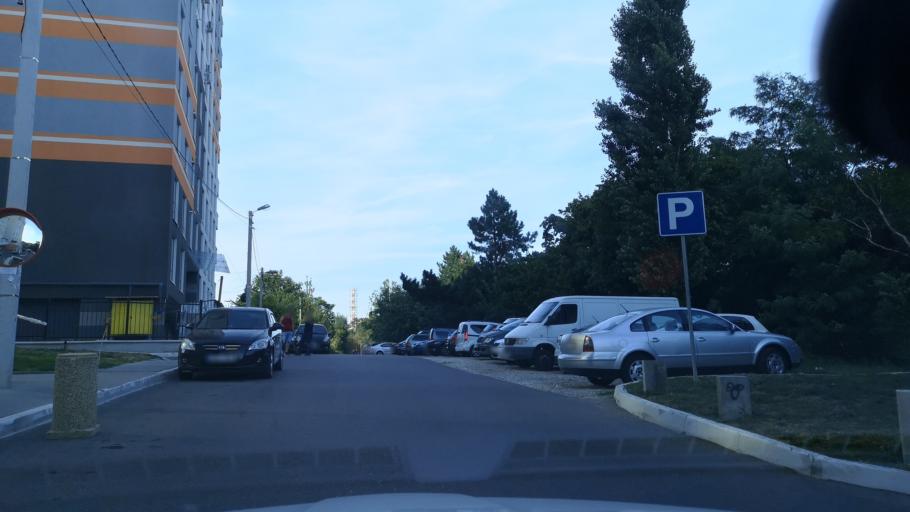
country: MD
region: Chisinau
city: Chisinau
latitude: 47.0029
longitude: 28.8451
